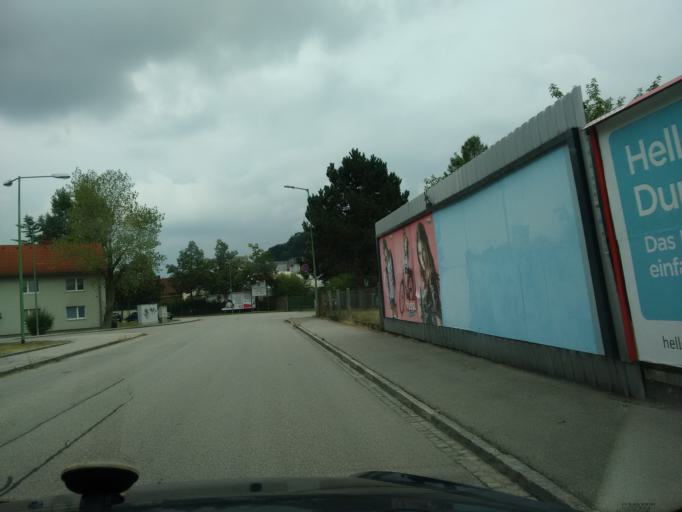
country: AT
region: Upper Austria
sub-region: Wels Stadt
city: Wels
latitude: 48.1620
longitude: 14.0609
